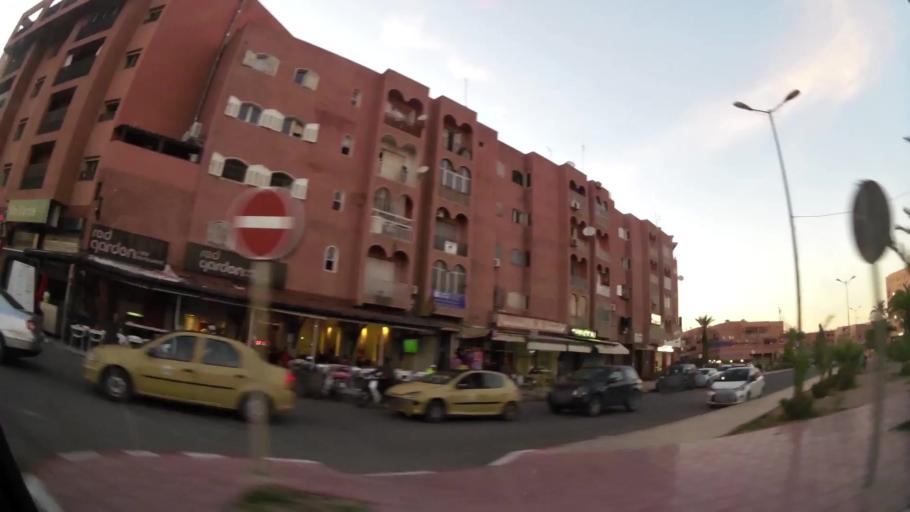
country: MA
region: Marrakech-Tensift-Al Haouz
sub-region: Marrakech
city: Marrakesh
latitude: 31.6404
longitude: -8.0008
